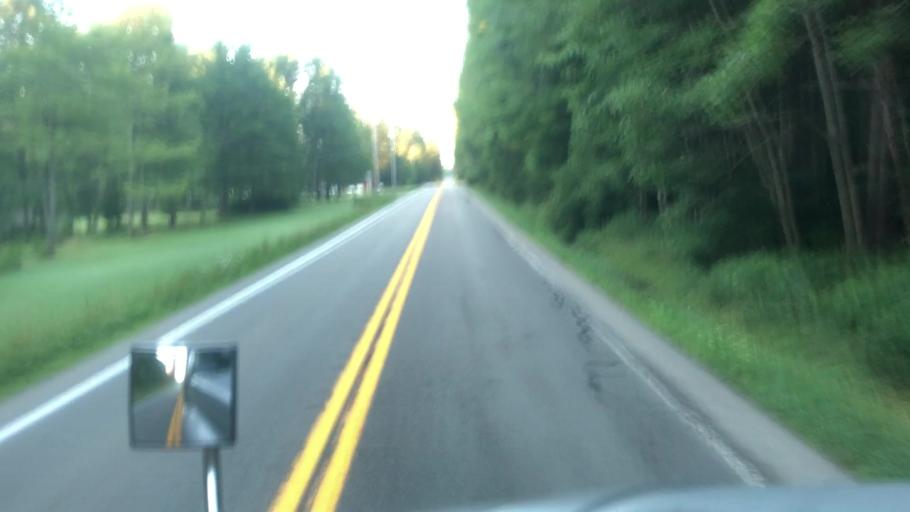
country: US
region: Pennsylvania
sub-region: Crawford County
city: Titusville
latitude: 41.5803
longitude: -79.6097
